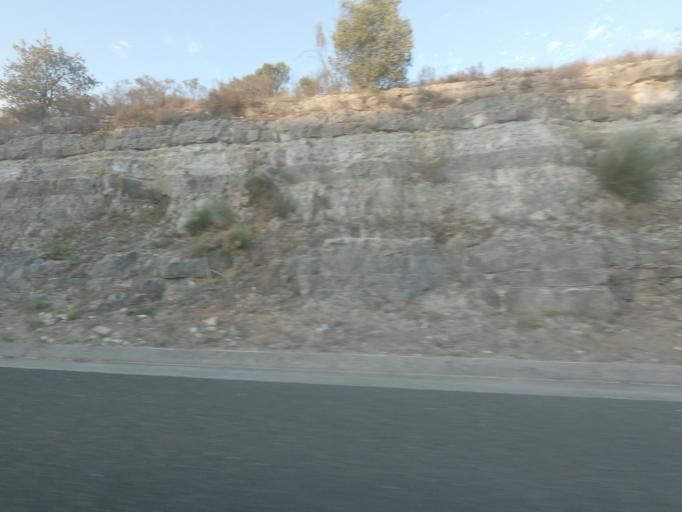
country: PT
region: Leiria
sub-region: Leiria
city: Santa Catarina da Serra
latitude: 39.6899
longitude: -8.6899
